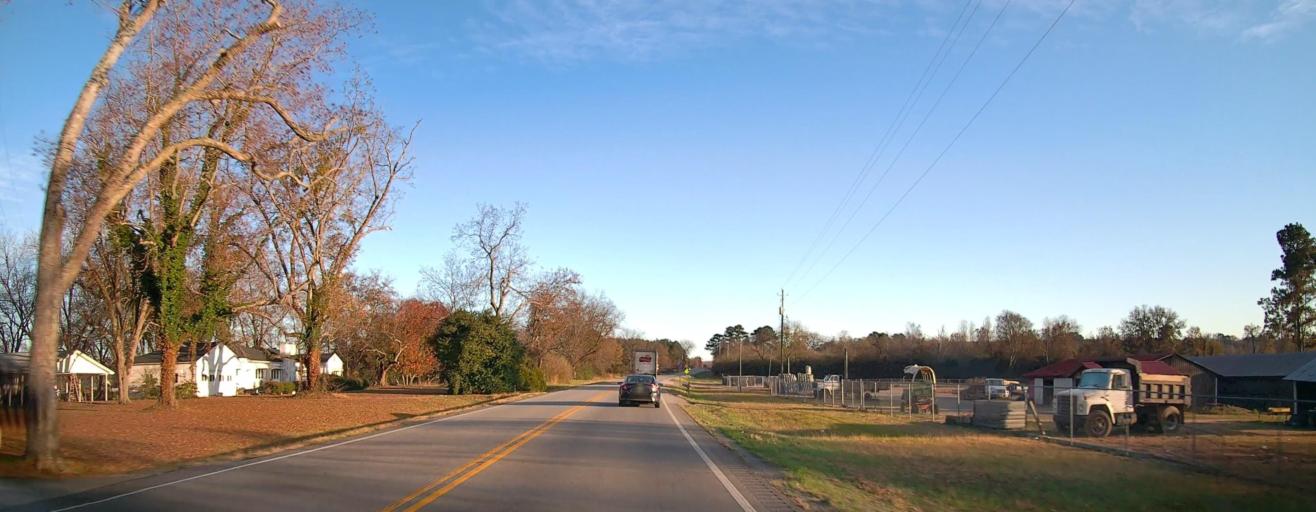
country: US
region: Alabama
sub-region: Blount County
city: Oneonta
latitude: 34.0948
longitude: -86.3566
